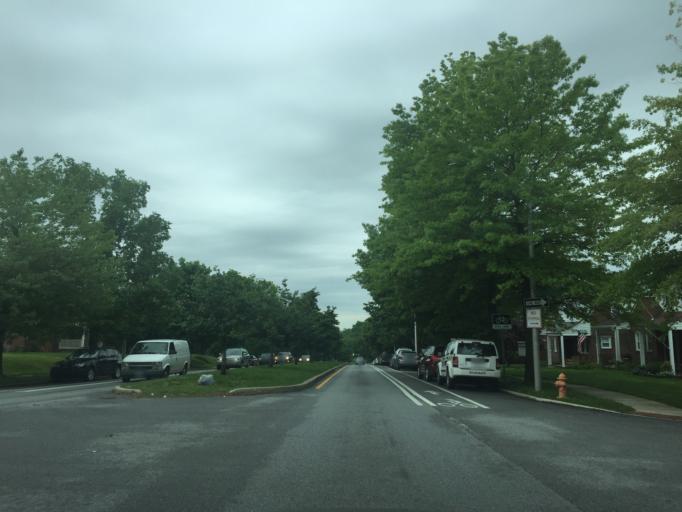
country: US
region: Maryland
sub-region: Baltimore County
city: Parkville
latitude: 39.3410
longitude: -76.5647
